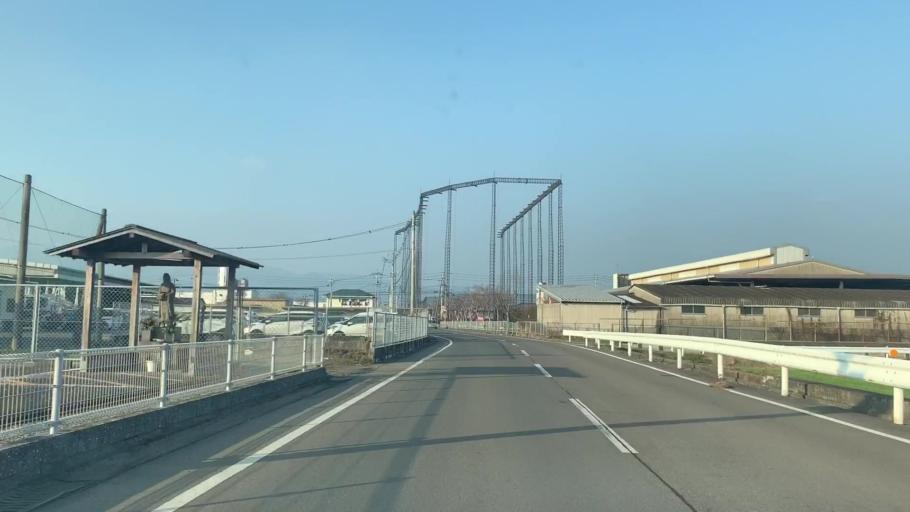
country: JP
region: Saga Prefecture
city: Saga-shi
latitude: 33.2635
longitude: 130.2479
